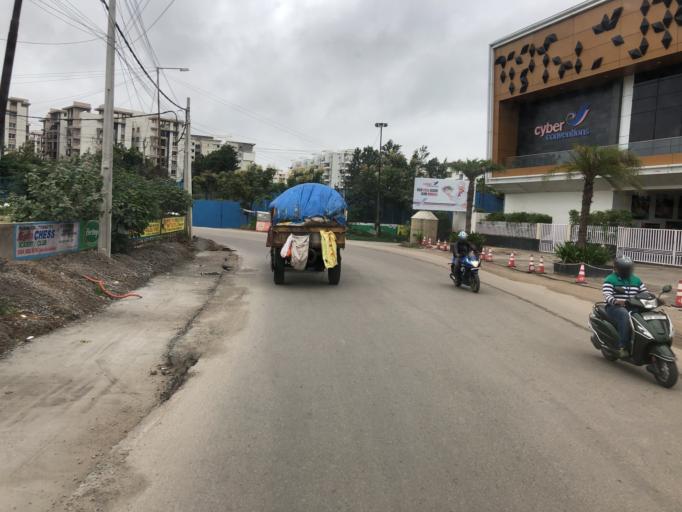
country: IN
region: Telangana
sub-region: Rangareddi
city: Kukatpalli
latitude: 17.4656
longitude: 78.3732
